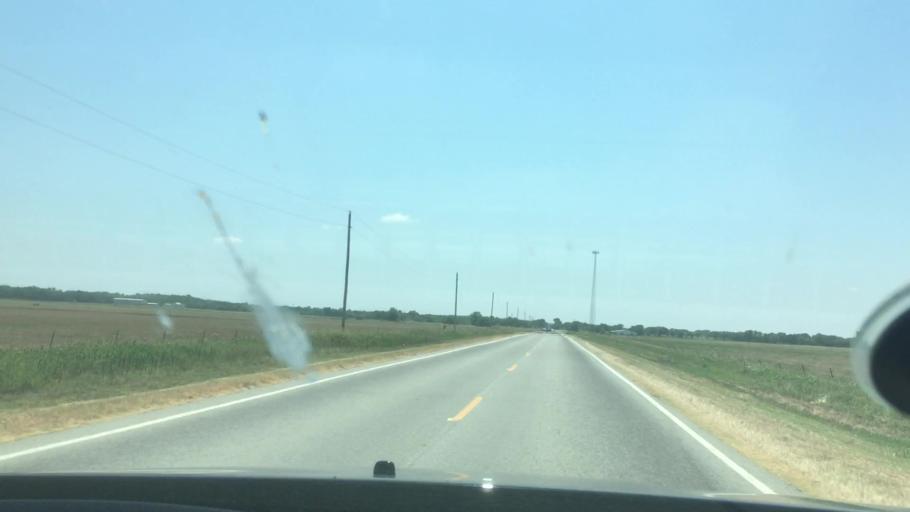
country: US
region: Oklahoma
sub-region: Coal County
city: Coalgate
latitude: 34.5115
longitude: -96.4070
